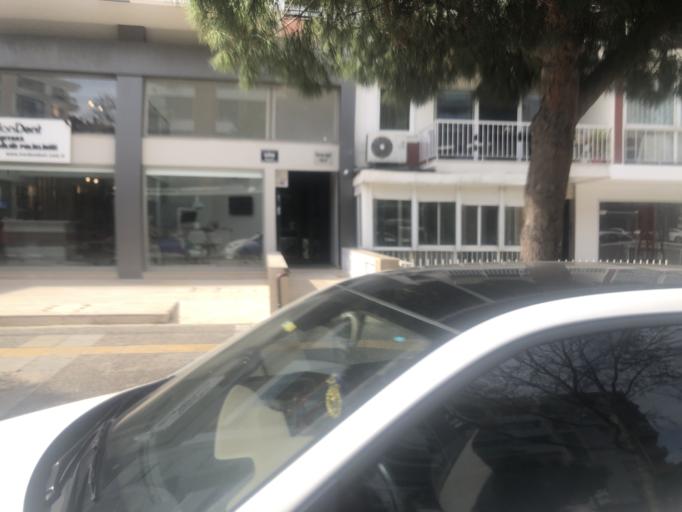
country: TR
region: Izmir
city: Karsiyaka
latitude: 38.4526
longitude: 27.1049
